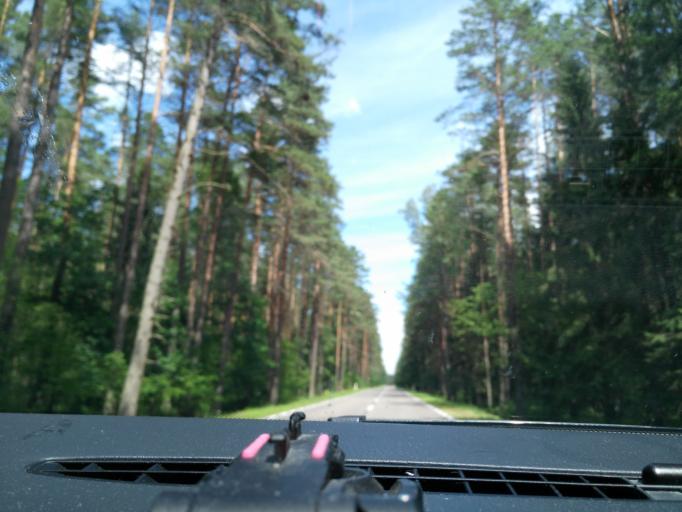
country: PL
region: Podlasie
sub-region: Powiat sejnenski
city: Krasnopol
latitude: 53.9685
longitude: 23.2483
